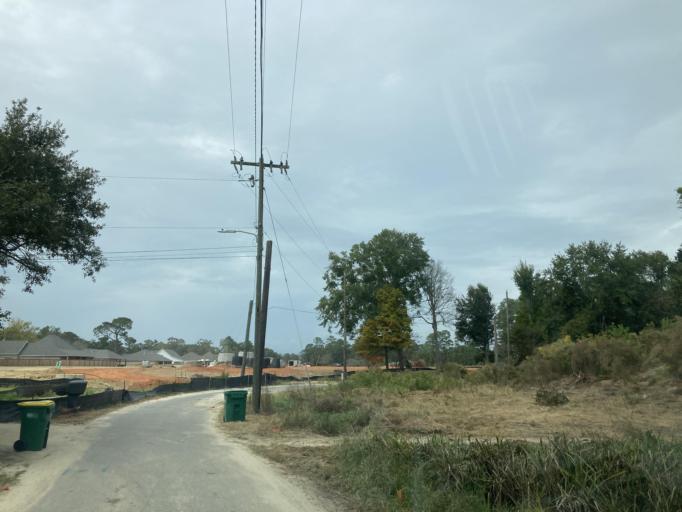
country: US
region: Mississippi
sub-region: Jackson County
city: Gulf Hills
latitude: 30.4324
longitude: -88.8365
